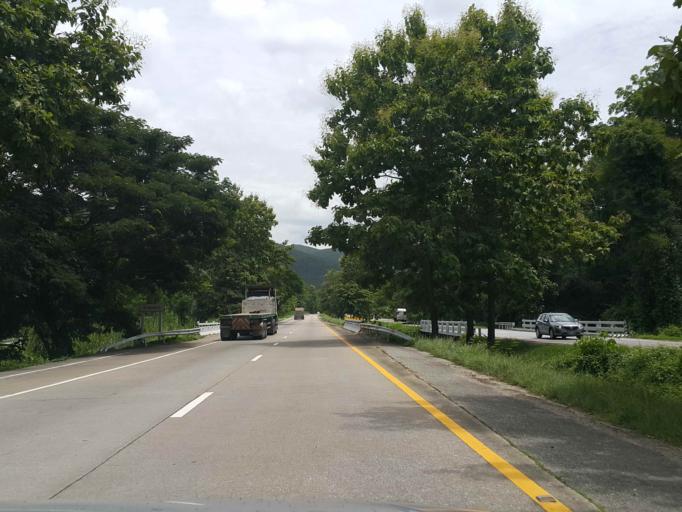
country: TH
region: Lamphun
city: Mae Tha
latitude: 18.5096
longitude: 99.1287
